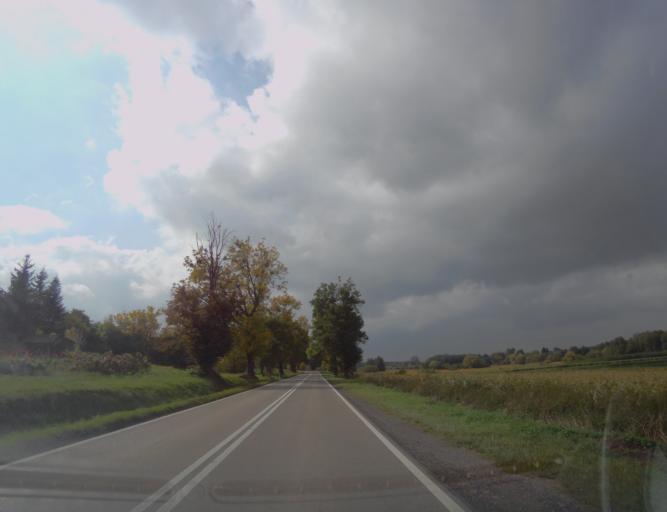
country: PL
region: Lublin Voivodeship
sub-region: Powiat krasnostawski
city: Gorzkow
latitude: 50.9422
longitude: 23.0100
